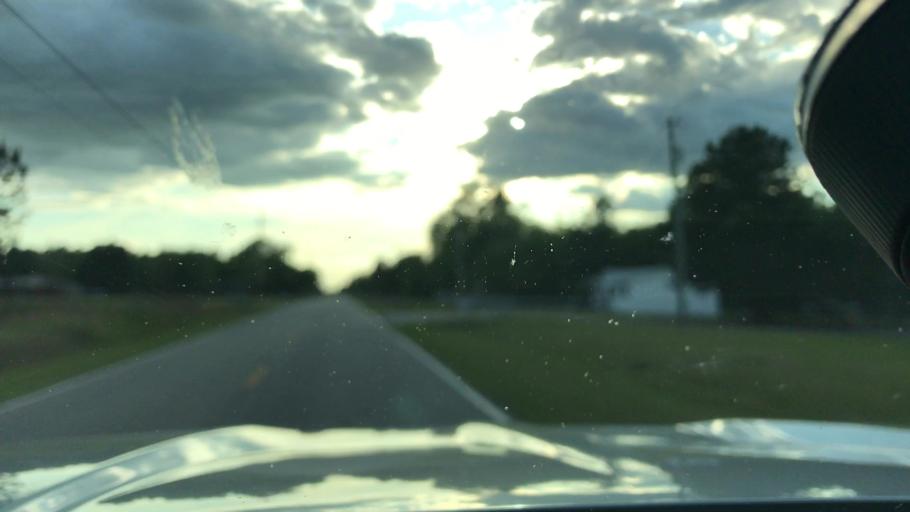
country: US
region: South Carolina
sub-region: Barnwell County
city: Blackville
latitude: 33.4743
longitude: -81.1802
